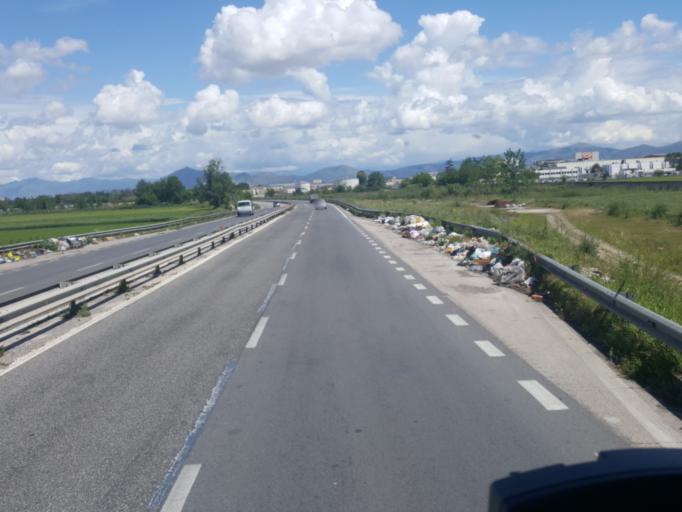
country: IT
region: Campania
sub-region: Provincia di Napoli
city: Pascarola
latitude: 40.9782
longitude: 14.2935
